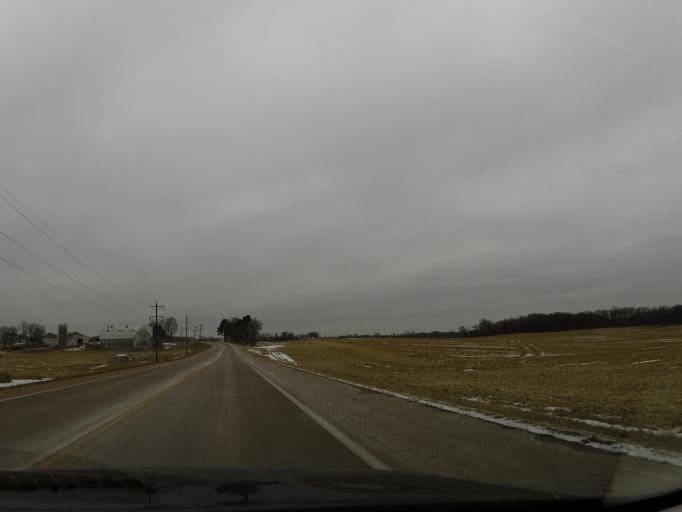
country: US
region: Minnesota
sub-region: Carver County
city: Watertown
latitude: 44.9108
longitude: -93.8225
